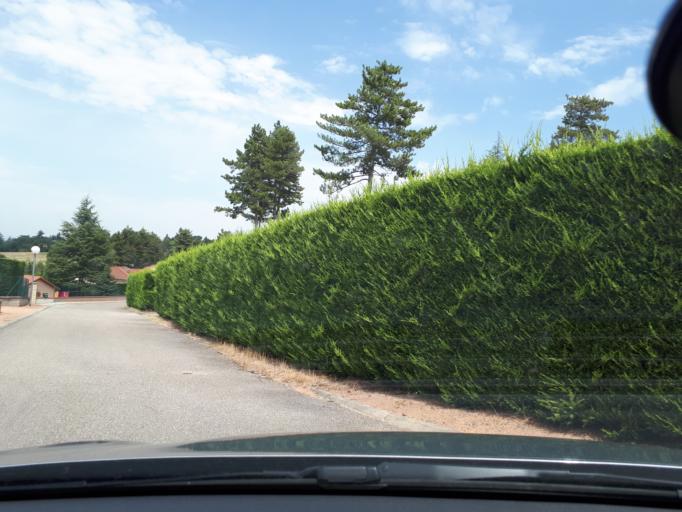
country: FR
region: Rhone-Alpes
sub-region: Departement de la Loire
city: Civens
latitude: 45.7586
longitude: 4.2777
